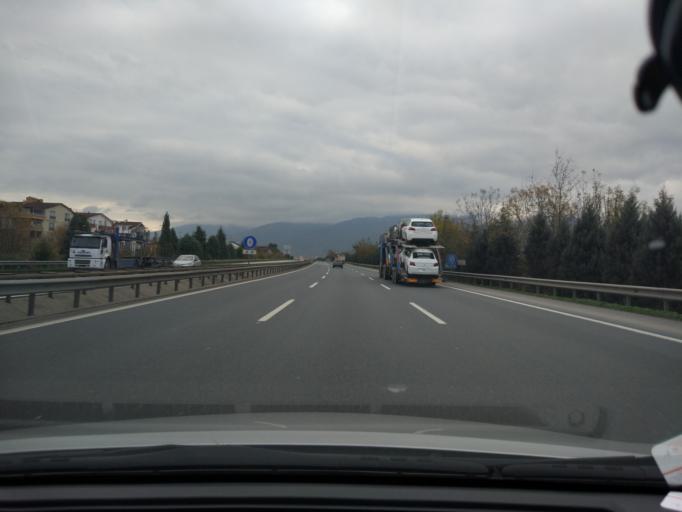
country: TR
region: Kocaeli
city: Kosekoy
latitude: 40.7397
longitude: 30.0460
